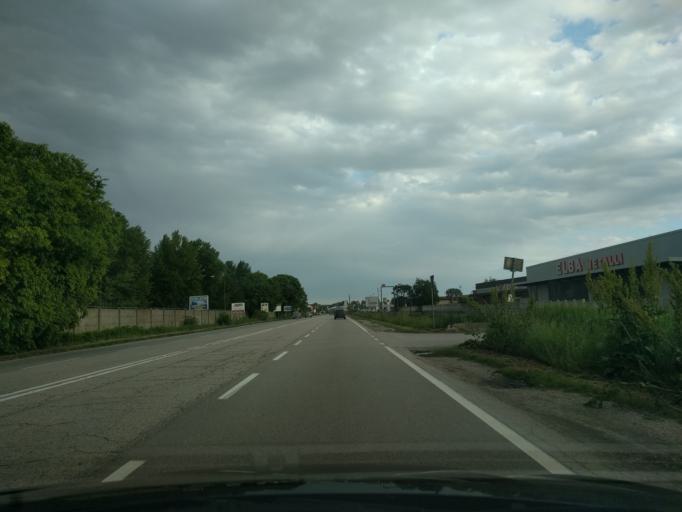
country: IT
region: Emilia-Romagna
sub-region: Provincia di Ferrara
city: Ferrara
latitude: 44.8556
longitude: 11.5841
